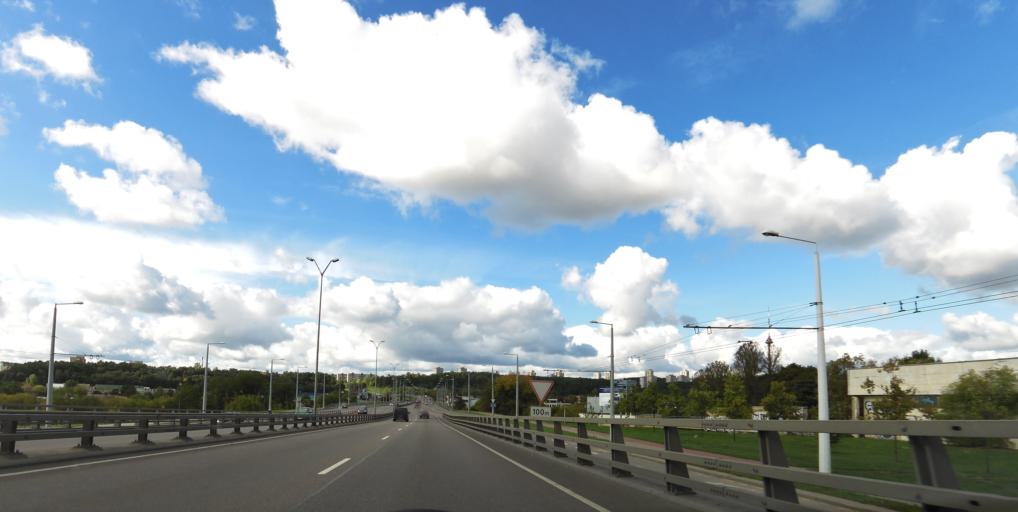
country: LT
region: Vilnius County
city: Vilkpede
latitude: 54.6695
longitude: 25.2342
